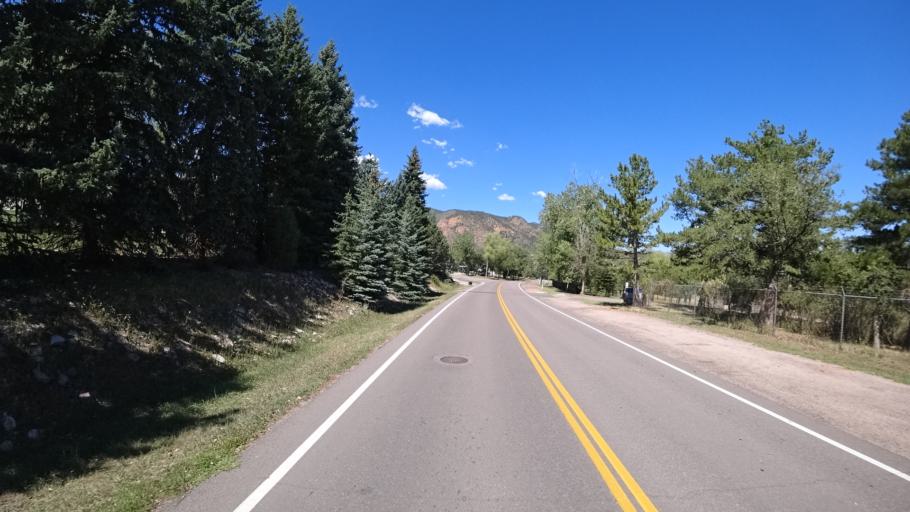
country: US
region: Colorado
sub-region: El Paso County
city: Colorado Springs
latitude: 38.7865
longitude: -104.8588
